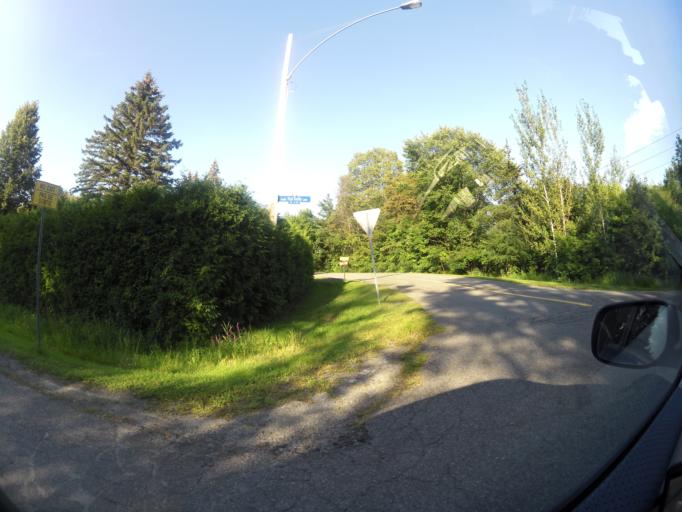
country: CA
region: Ontario
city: Clarence-Rockland
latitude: 45.5103
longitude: -75.4610
